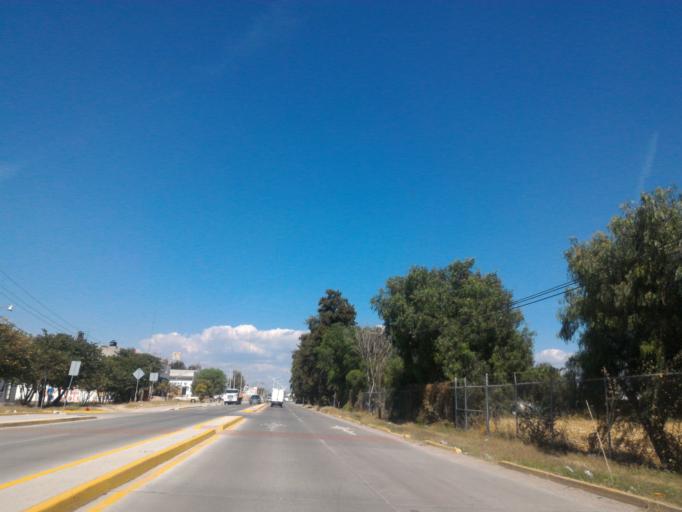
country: MX
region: Guanajuato
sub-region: San Francisco del Rincon
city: Fraccionamiento Villa Jardin
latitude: 21.0009
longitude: -101.8523
